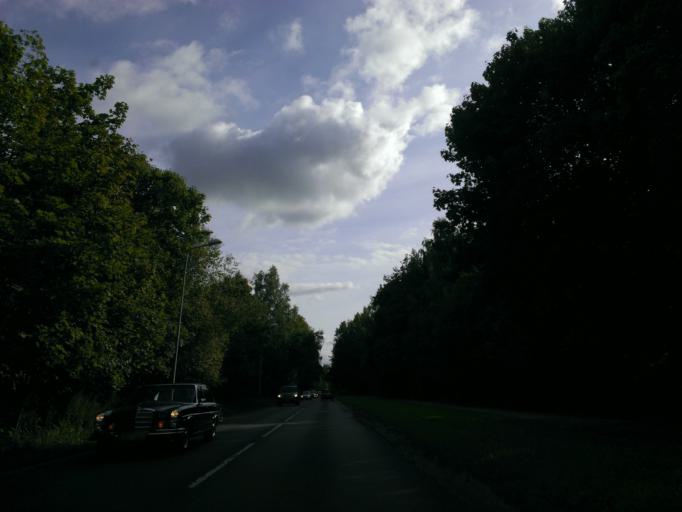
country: LV
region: Riga
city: Bergi
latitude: 56.9736
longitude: 24.2543
